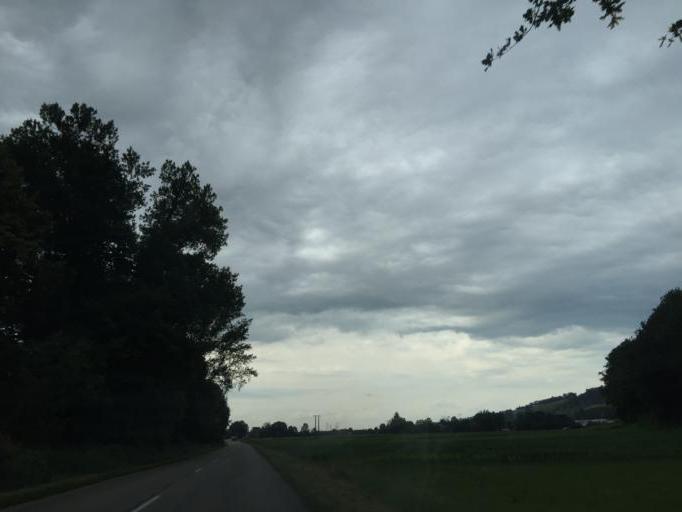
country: FR
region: Rhone-Alpes
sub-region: Departement de la Savoie
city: Le Pont-de-Beauvoisin
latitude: 45.5636
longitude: 5.6706
